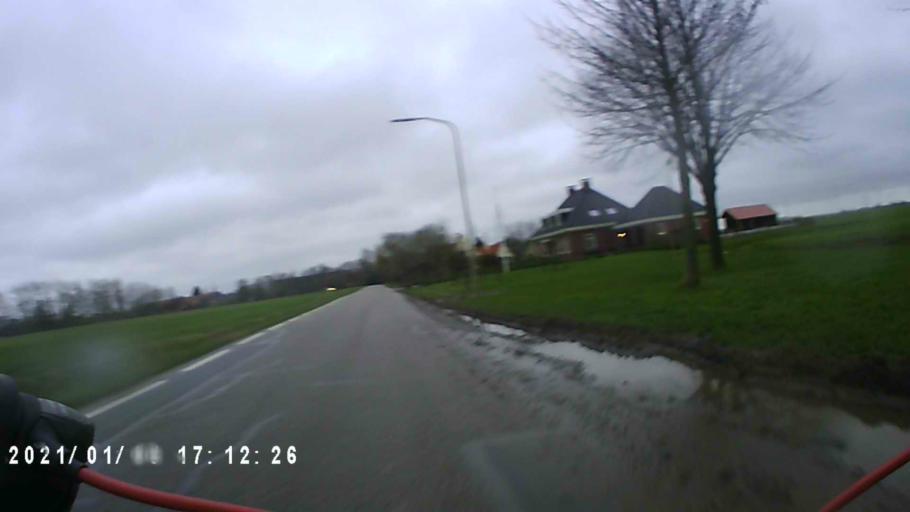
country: NL
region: Groningen
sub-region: Gemeente Delfzijl
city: Delfzijl
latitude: 53.2480
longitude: 6.9915
